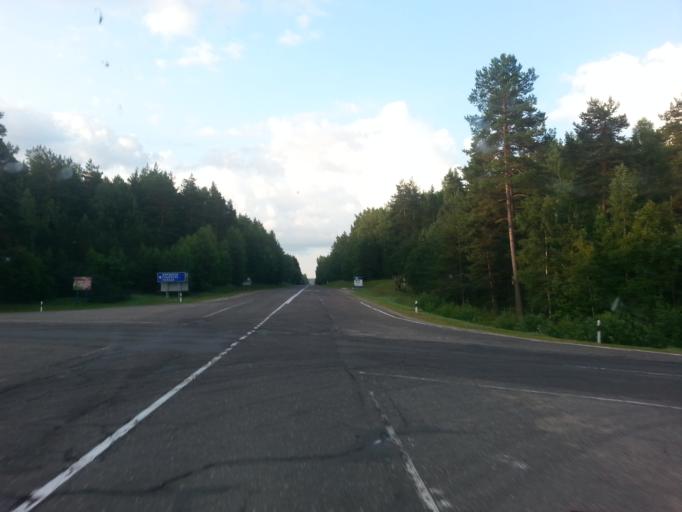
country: BY
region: Minsk
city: Kryvichy
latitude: 54.5890
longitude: 27.1937
